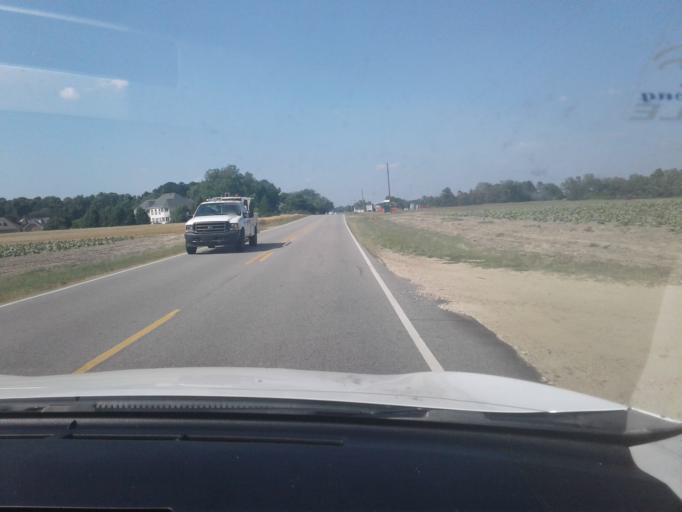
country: US
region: North Carolina
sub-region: Harnett County
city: Erwin
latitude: 35.3600
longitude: -78.6360
